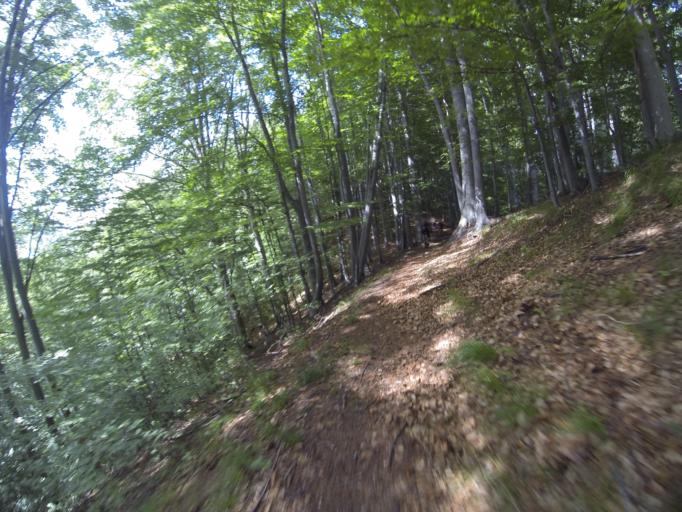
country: RO
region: Valcea
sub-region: Oras Baile Olanesti
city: Cheia
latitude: 45.2390
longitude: 24.1710
